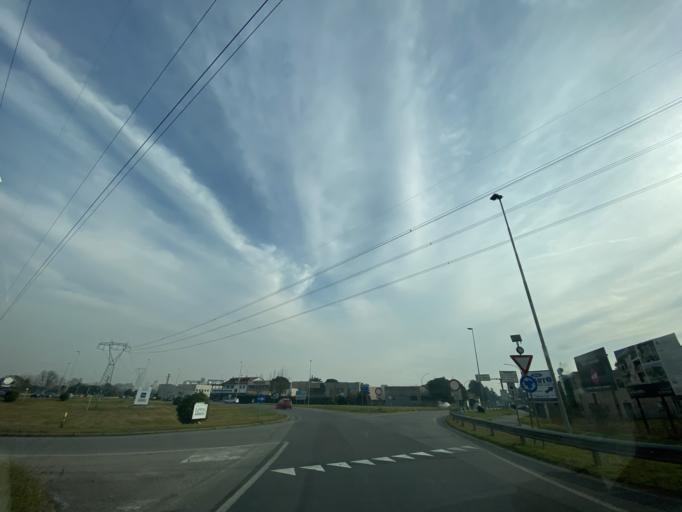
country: IT
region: Lombardy
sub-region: Citta metropolitana di Milano
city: Carugate
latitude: 45.5389
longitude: 9.3370
